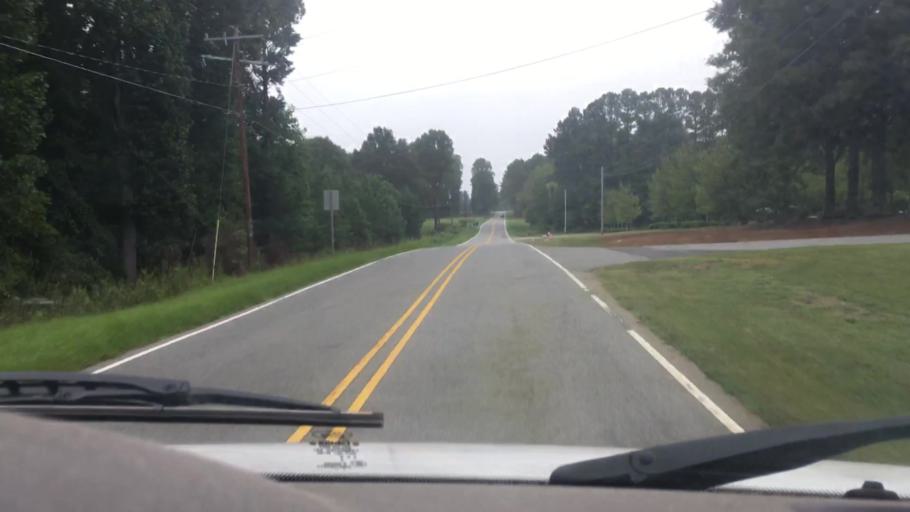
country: US
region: North Carolina
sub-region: Gaston County
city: Davidson
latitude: 35.4717
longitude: -80.7539
